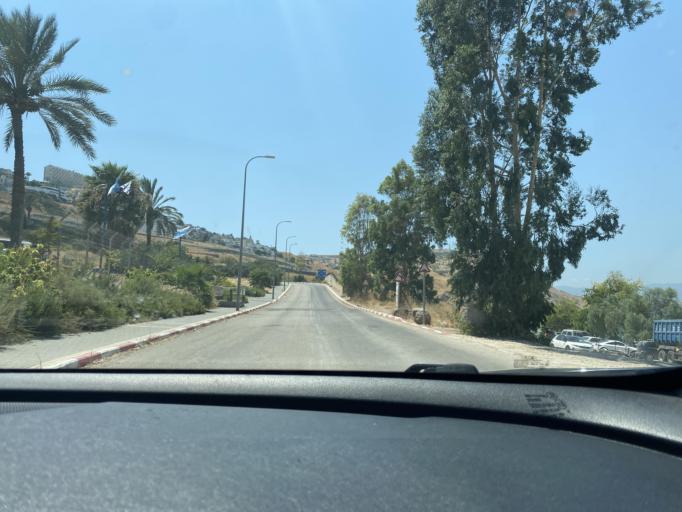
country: IL
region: Northern District
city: Tiberias
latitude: 32.8017
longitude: 35.5336
